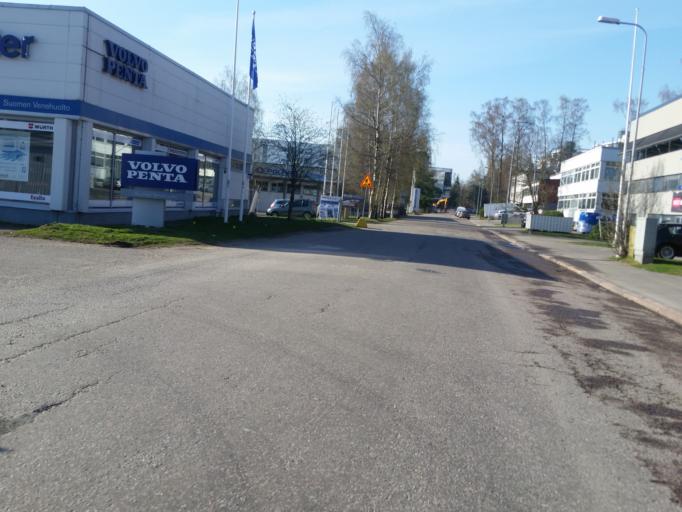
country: FI
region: Uusimaa
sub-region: Helsinki
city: Helsinki
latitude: 60.1510
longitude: 24.8879
